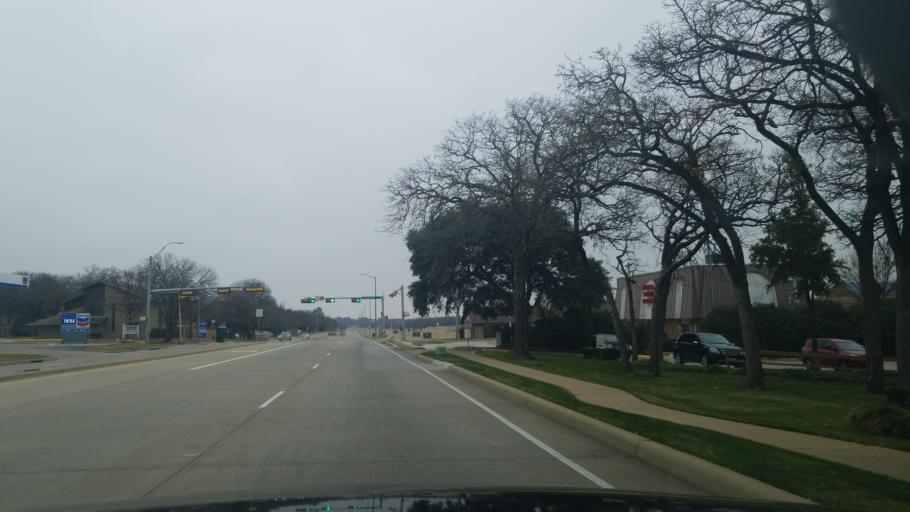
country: US
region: Texas
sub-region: Denton County
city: Denton
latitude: 33.1908
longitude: -97.1245
